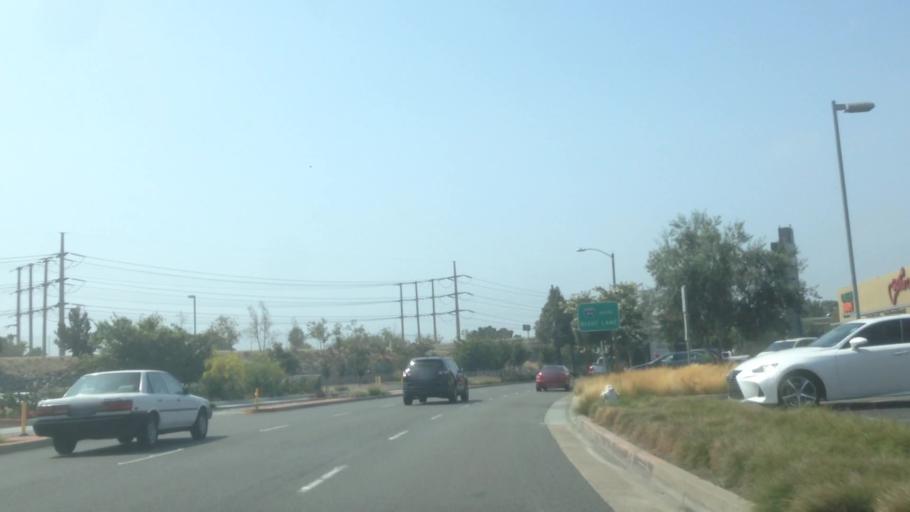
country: US
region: California
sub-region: Orange County
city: Fountain Valley
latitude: 33.6974
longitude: -117.9348
